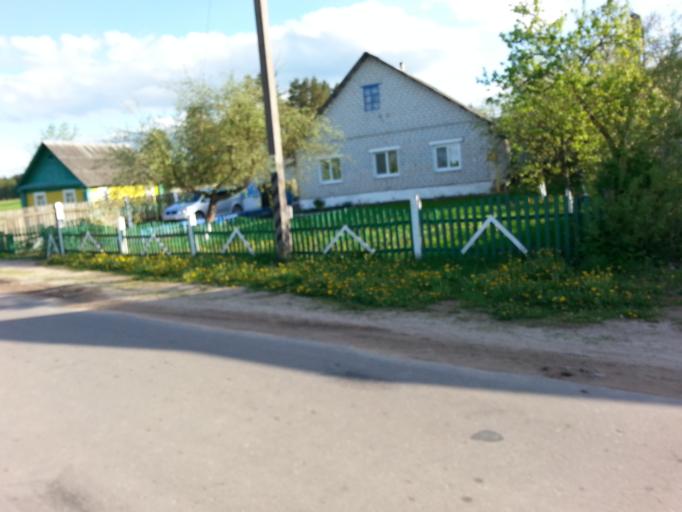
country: BY
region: Minsk
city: Narach
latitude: 54.9337
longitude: 26.7037
